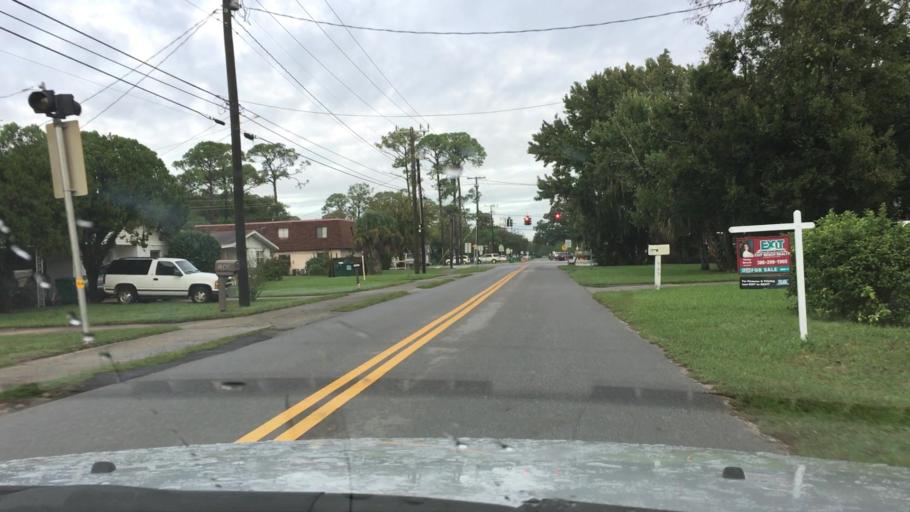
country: US
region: Florida
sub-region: Volusia County
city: Holly Hill
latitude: 29.2511
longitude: -81.0550
